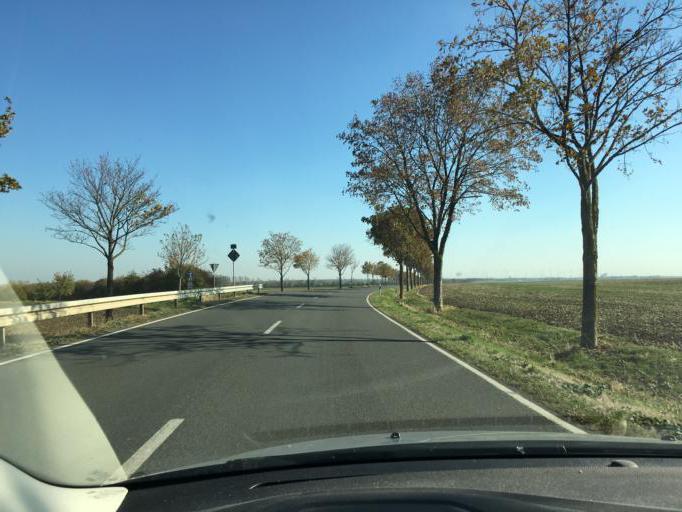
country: DE
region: Saxony-Anhalt
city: Wanzleben
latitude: 52.0337
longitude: 11.4731
